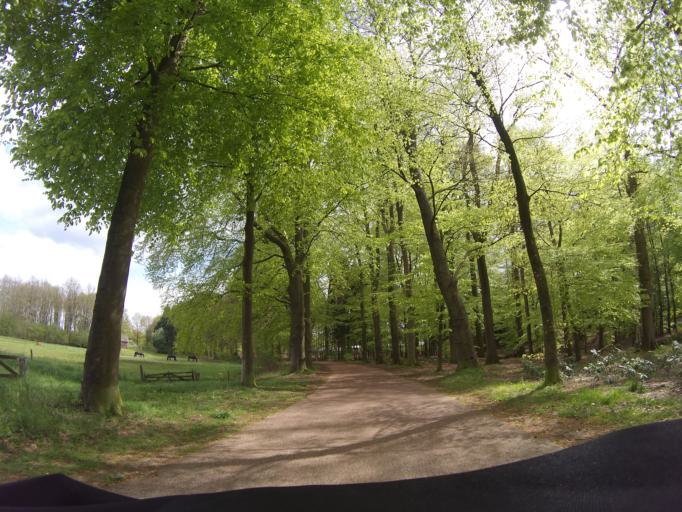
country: NL
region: Overijssel
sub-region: Gemeente Twenterand
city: Den Ham
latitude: 52.5119
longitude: 6.4153
